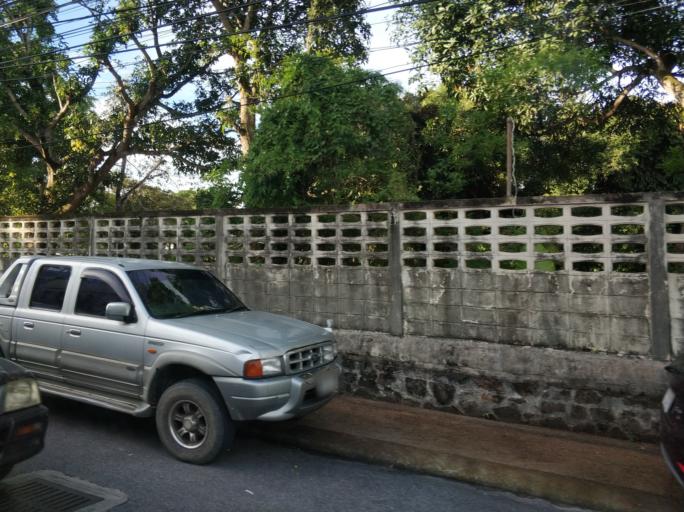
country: TH
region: Phuket
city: Ban Talat Nua
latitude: 7.8853
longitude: 98.3784
